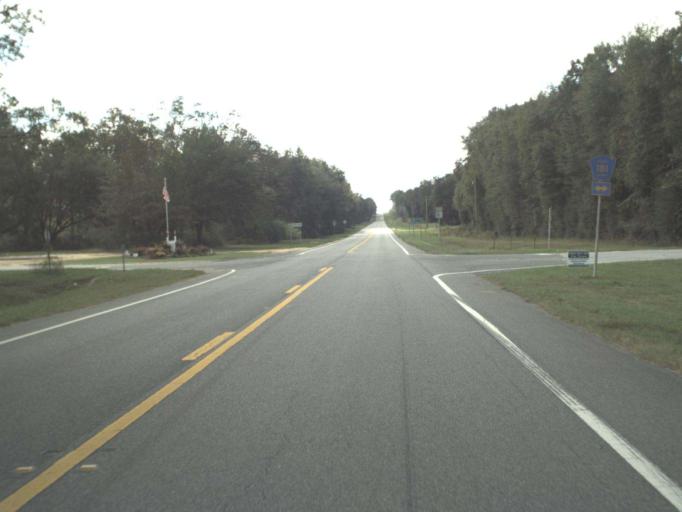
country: US
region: Alabama
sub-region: Geneva County
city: Geneva
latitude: 30.8518
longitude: -85.9468
